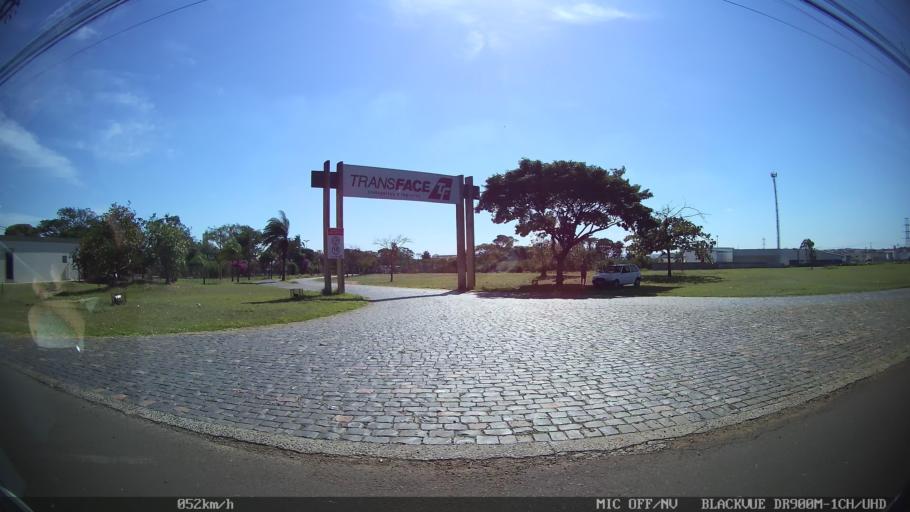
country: BR
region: Sao Paulo
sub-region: Franca
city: Franca
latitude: -20.5474
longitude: -47.4362
